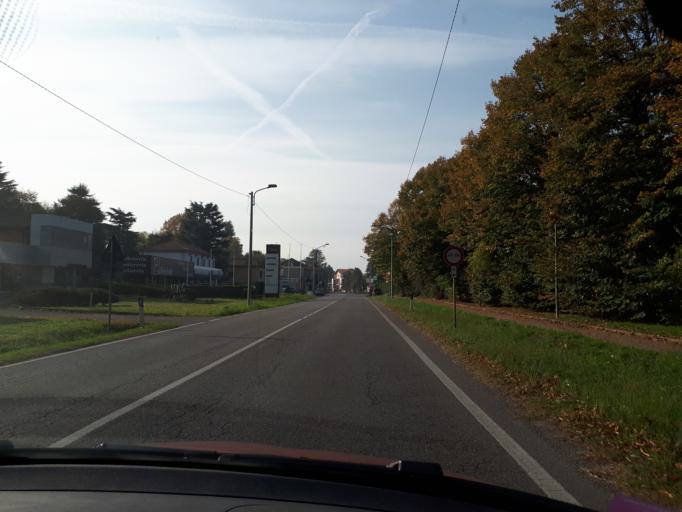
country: IT
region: Lombardy
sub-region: Provincia di Monza e Brianza
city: Lesmo
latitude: 45.6533
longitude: 9.3092
